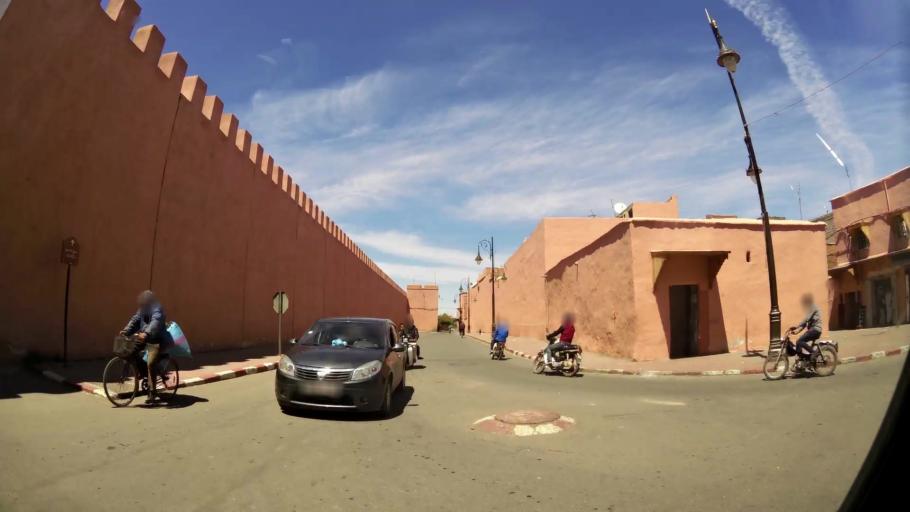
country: MA
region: Marrakech-Tensift-Al Haouz
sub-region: Marrakech
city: Marrakesh
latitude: 31.6142
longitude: -7.9796
